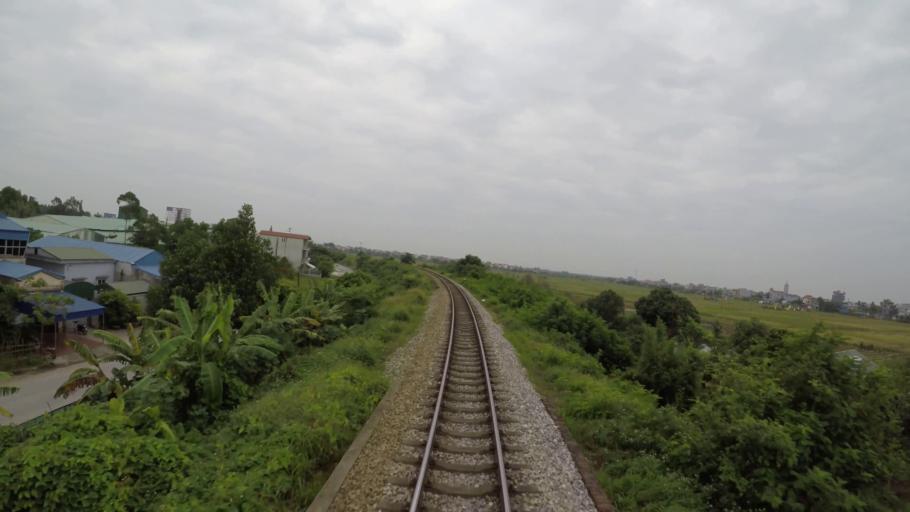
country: VN
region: Hai Duong
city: Thanh Pho Hai Duong
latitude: 20.9578
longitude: 106.3672
